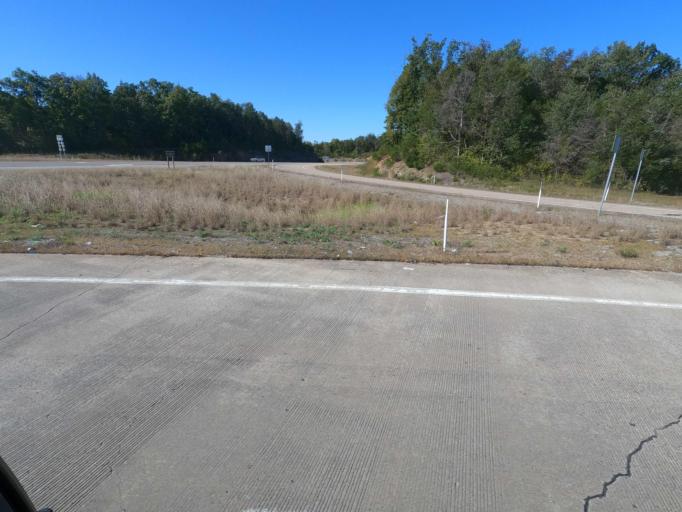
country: US
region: Tennessee
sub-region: Wilson County
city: Rural Hill
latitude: 36.0404
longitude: -86.4297
